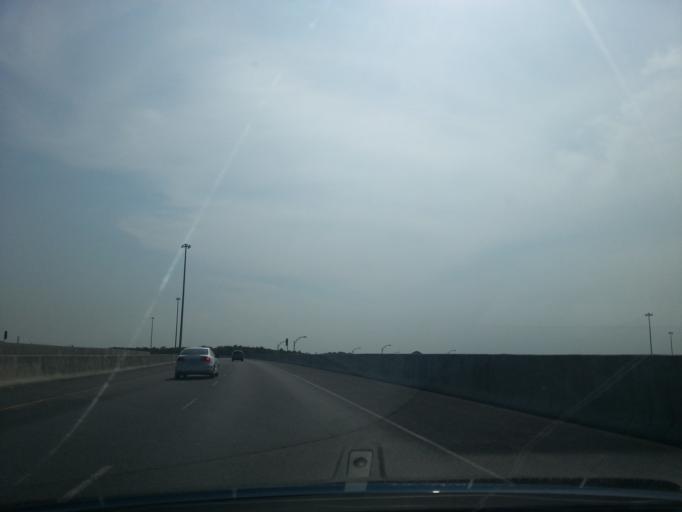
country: CA
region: Quebec
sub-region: Monteregie
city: Candiac
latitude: 45.3759
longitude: -73.4953
